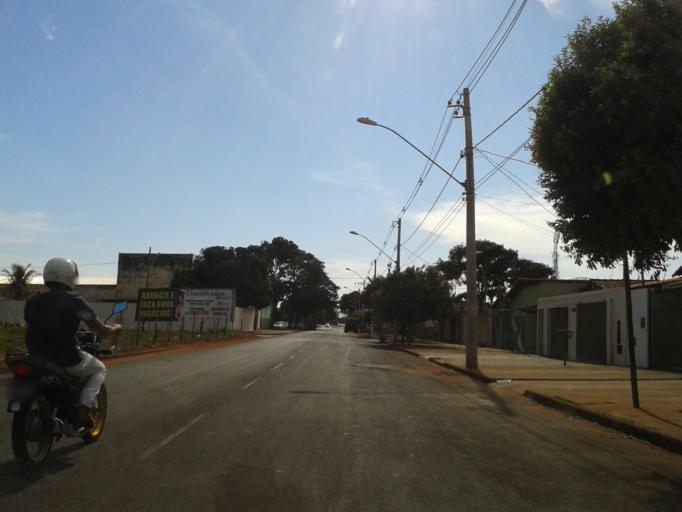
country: BR
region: Minas Gerais
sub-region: Ituiutaba
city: Ituiutaba
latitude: -18.9607
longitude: -49.4553
